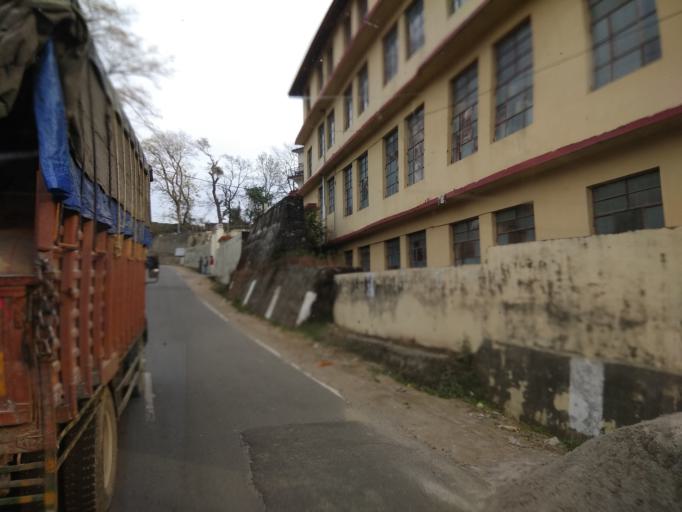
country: IN
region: Himachal Pradesh
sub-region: Kangra
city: Palampur
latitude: 32.1145
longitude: 76.5159
